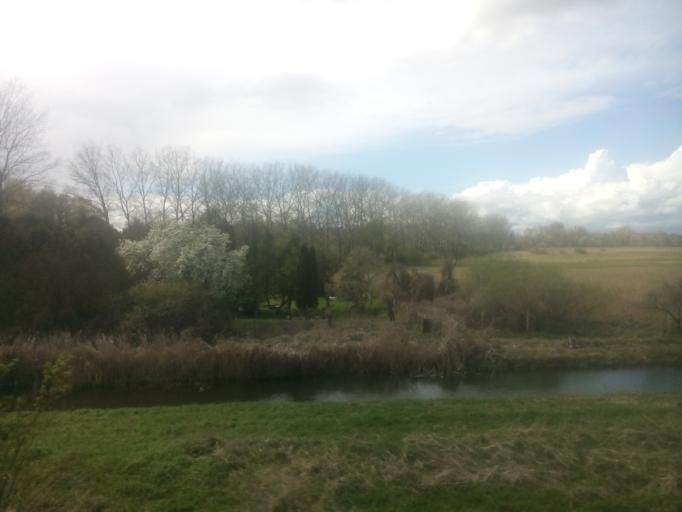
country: DE
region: Brandenburg
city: Kremmen
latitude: 52.7770
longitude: 13.0406
